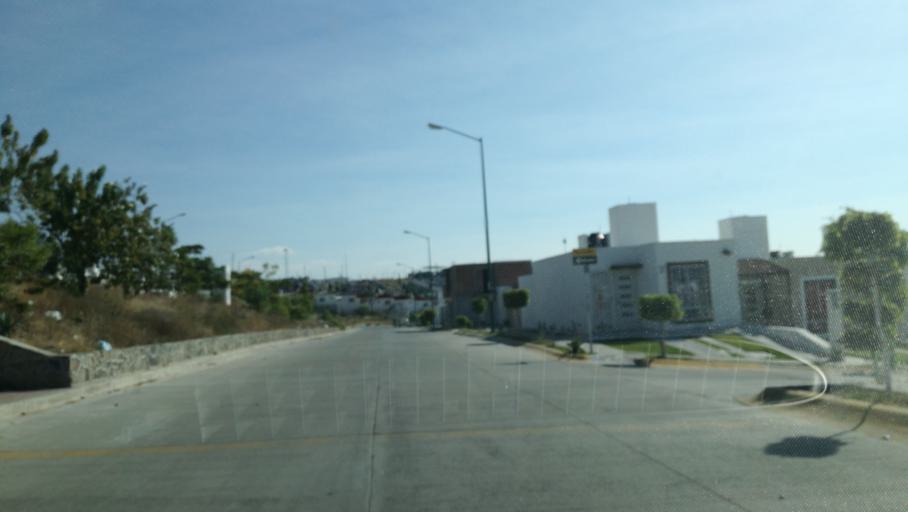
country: MX
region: Guanajuato
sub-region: Leon
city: La Ermita
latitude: 21.1594
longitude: -101.7401
